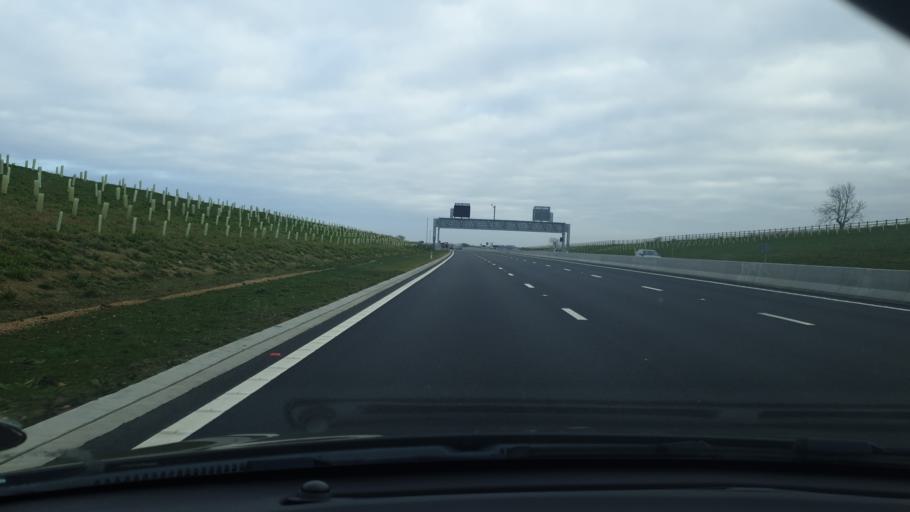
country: GB
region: England
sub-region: Cambridgeshire
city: Godmanchester
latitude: 52.2924
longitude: -0.1441
